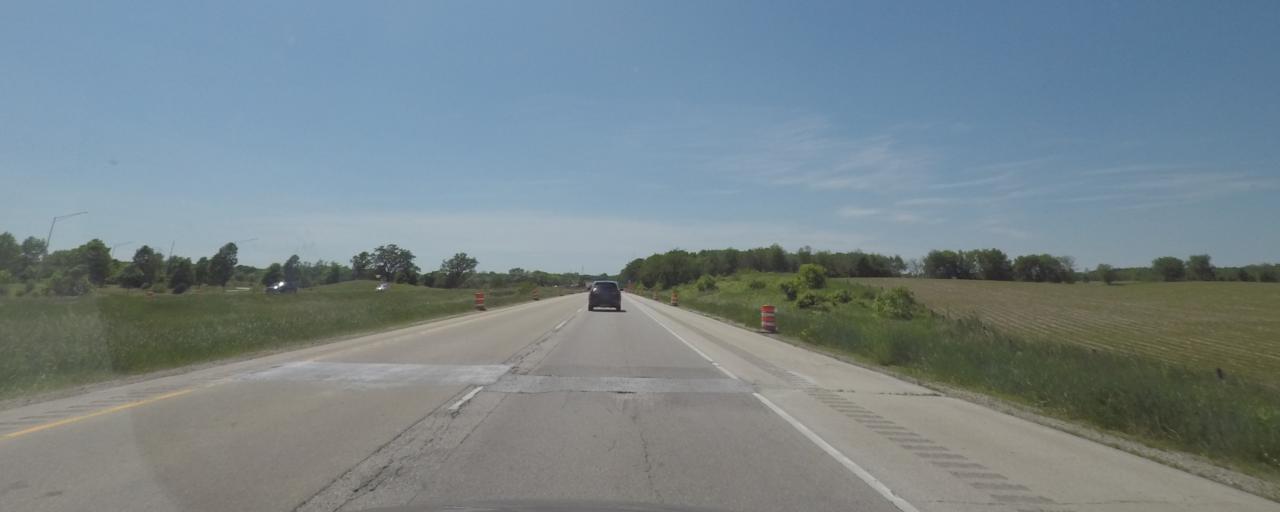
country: US
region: Wisconsin
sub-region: Jefferson County
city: Lake Mills
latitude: 43.0875
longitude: -88.8748
